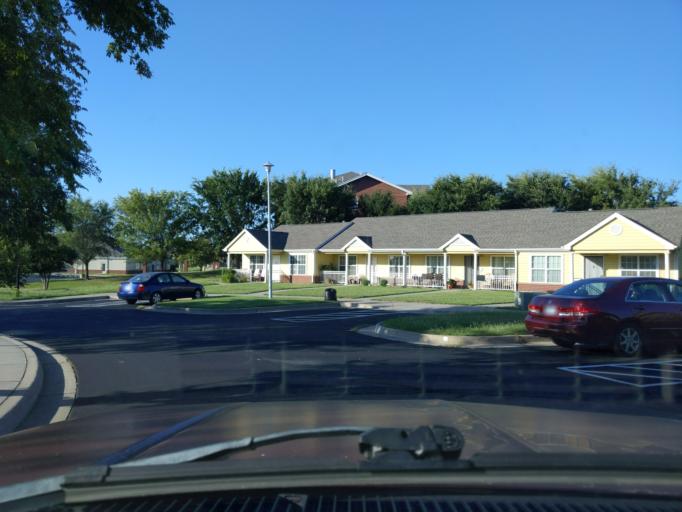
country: US
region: Oklahoma
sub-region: Tulsa County
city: Tulsa
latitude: 36.1676
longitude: -96.0018
